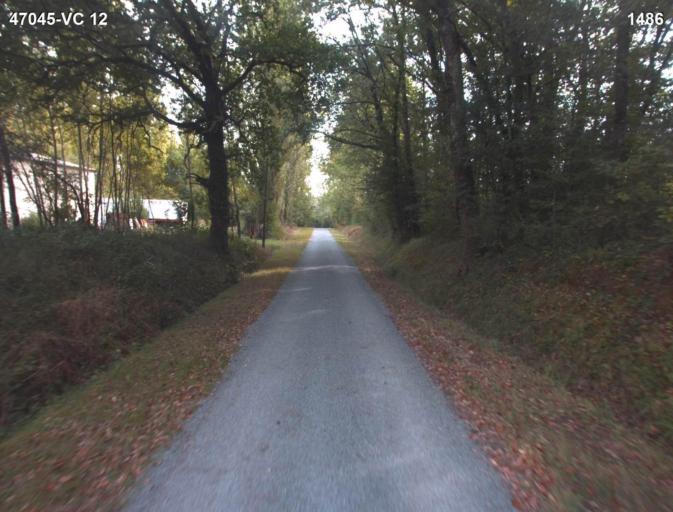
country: FR
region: Aquitaine
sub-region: Departement du Lot-et-Garonne
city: Nerac
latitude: 44.1456
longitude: 0.4319
